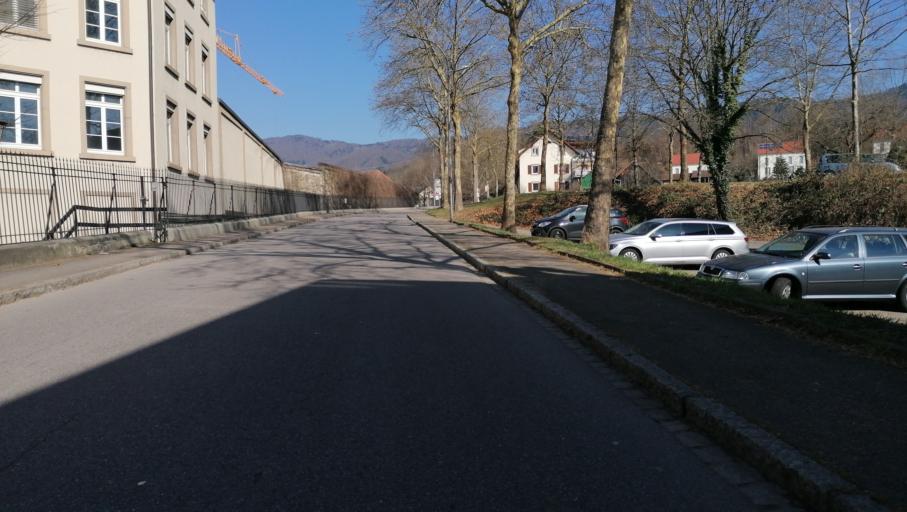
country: DE
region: Baden-Wuerttemberg
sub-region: Freiburg Region
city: Schworstadt
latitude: 47.5852
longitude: 7.9099
